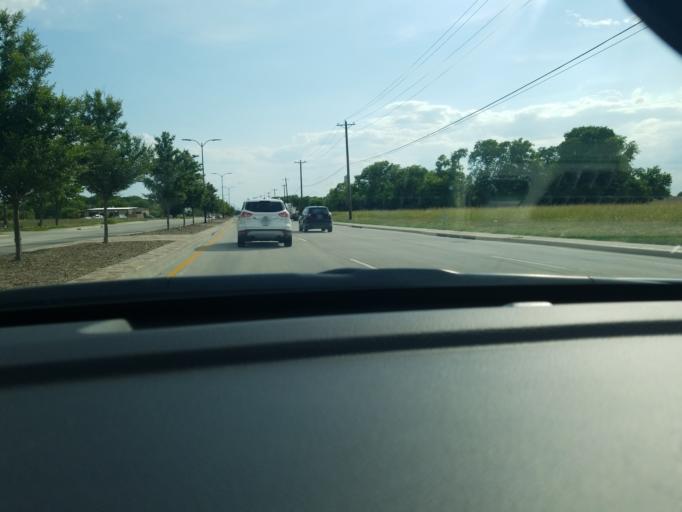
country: US
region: Texas
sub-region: Denton County
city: Little Elm
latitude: 33.1660
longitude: -96.9295
